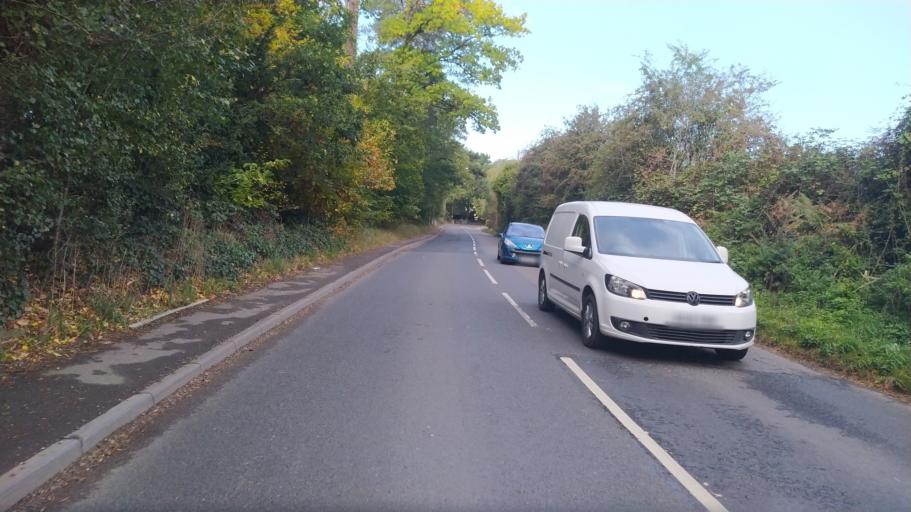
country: GB
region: England
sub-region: Hampshire
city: Eversley
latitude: 51.3582
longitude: -0.8912
